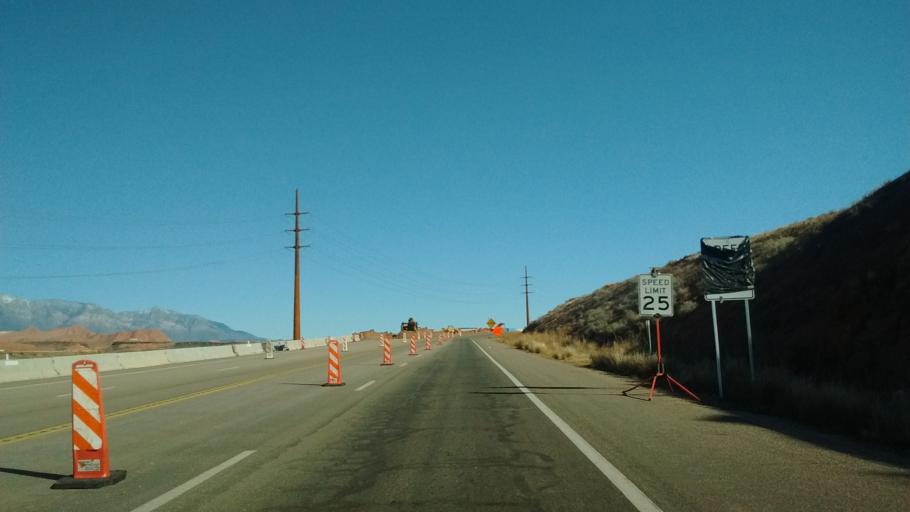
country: US
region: Utah
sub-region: Washington County
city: Washington
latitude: 37.1338
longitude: -113.4788
